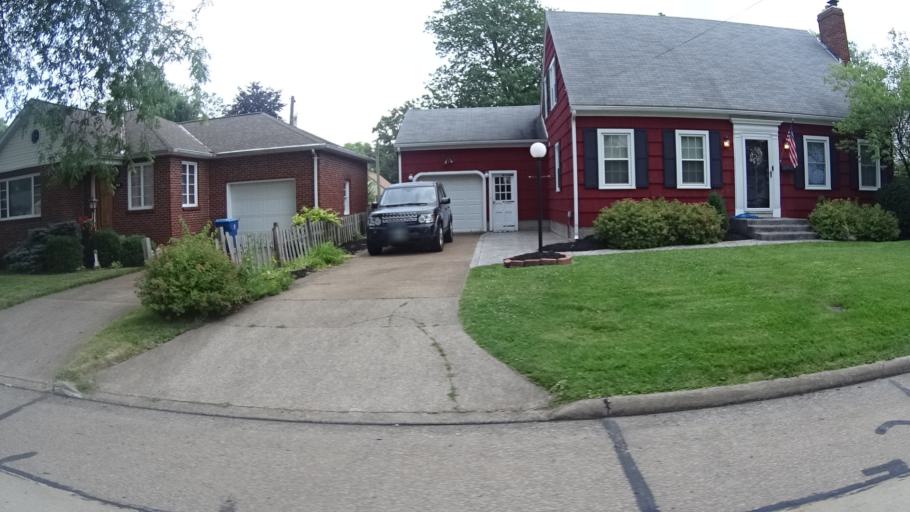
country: US
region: Ohio
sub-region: Erie County
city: Huron
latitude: 41.3898
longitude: -82.5402
